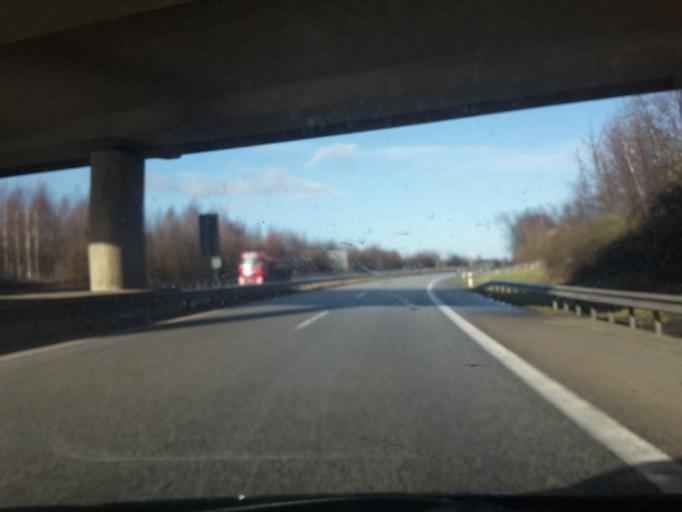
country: DE
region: Schleswig-Holstein
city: Oldenburg in Holstein
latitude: 54.2950
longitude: 10.8712
